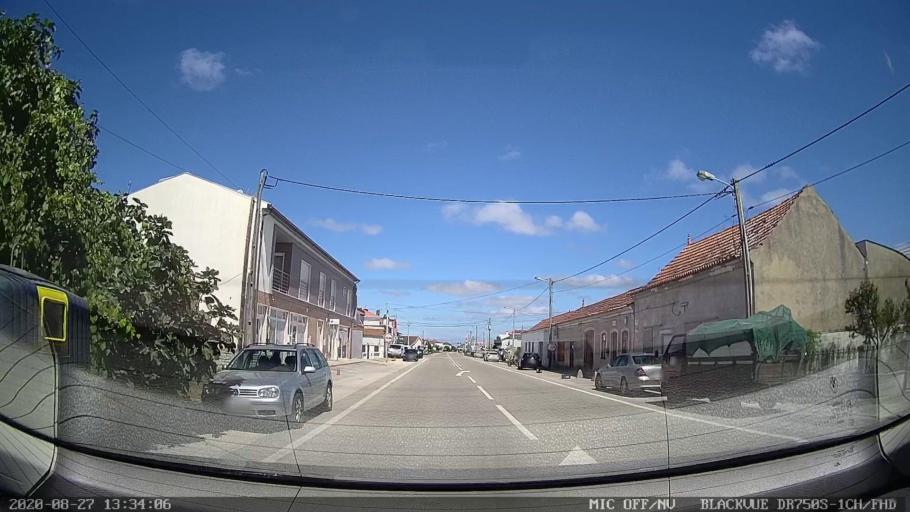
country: PT
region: Coimbra
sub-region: Mira
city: Mira
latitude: 40.4737
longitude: -8.6966
